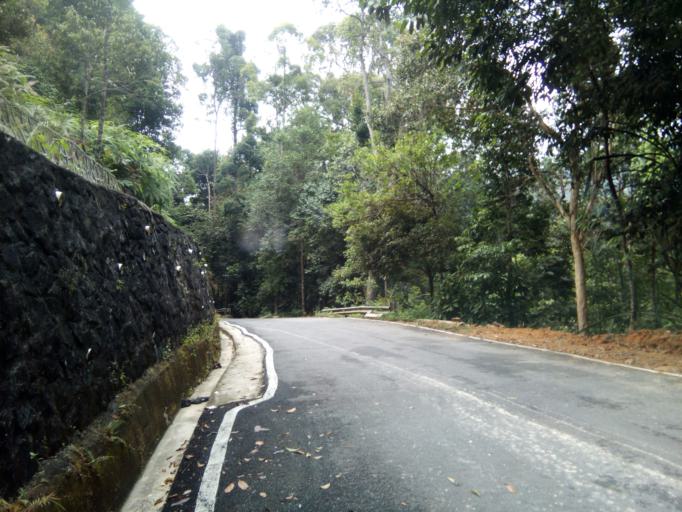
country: MY
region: Penang
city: Tanjung Tokong
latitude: 5.4359
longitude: 100.2818
